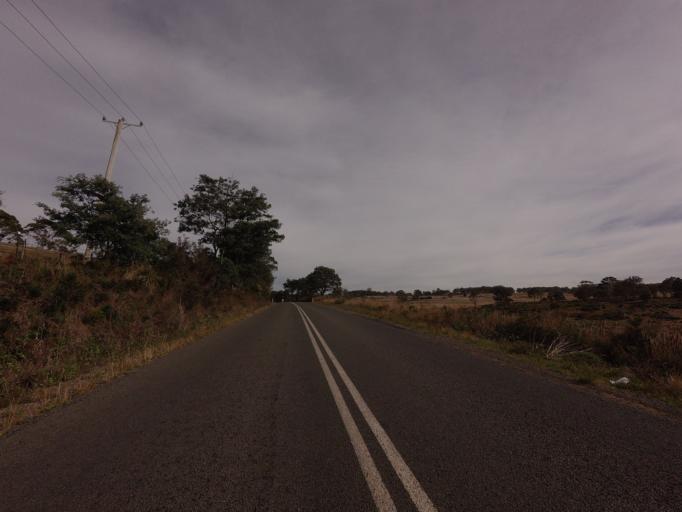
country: AU
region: Tasmania
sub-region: Sorell
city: Sorell
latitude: -42.4175
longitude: 147.4628
